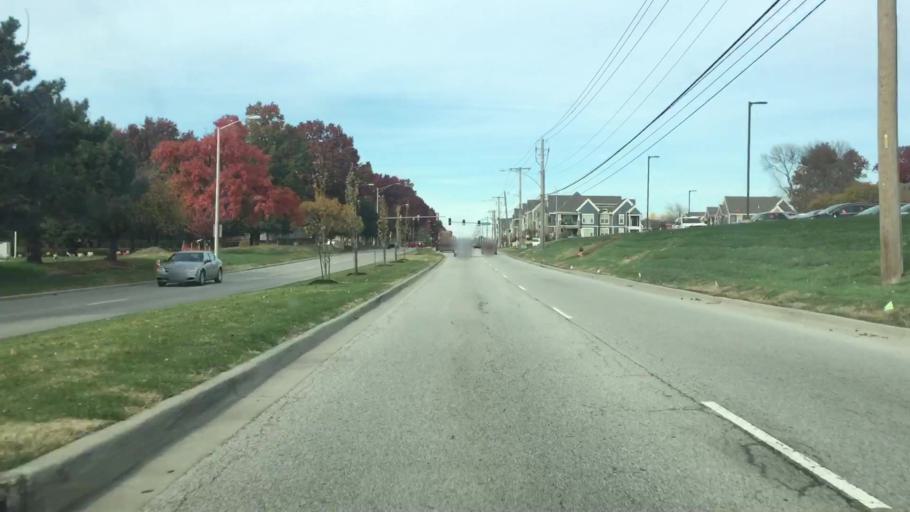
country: US
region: Kansas
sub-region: Johnson County
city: Lenexa
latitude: 38.9767
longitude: -94.7236
